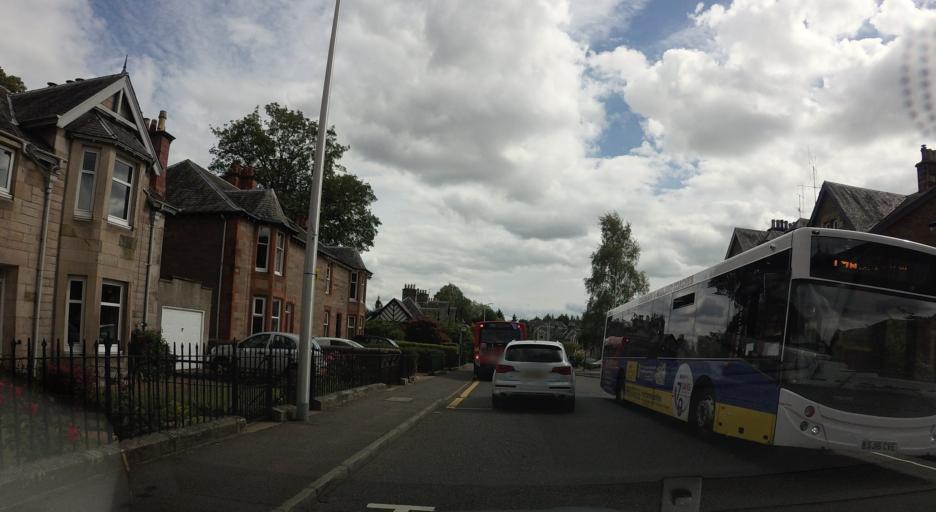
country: GB
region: Scotland
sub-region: Perth and Kinross
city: Perth
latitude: 56.3967
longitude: -3.4505
